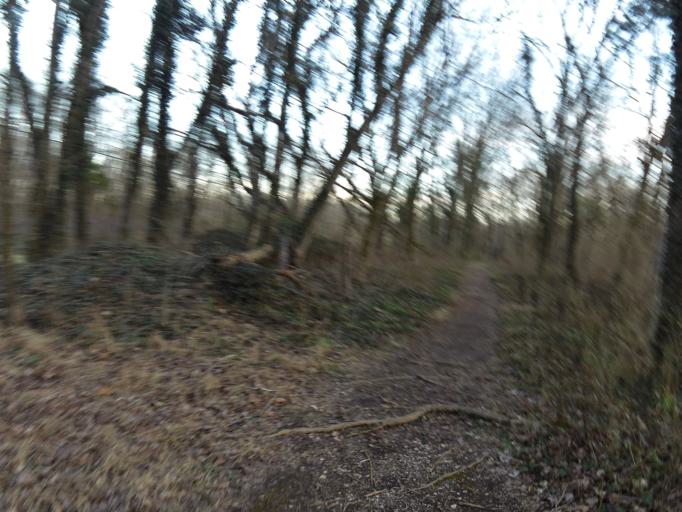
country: US
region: Tennessee
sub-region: Knox County
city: Knoxville
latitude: 35.9531
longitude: -83.8660
